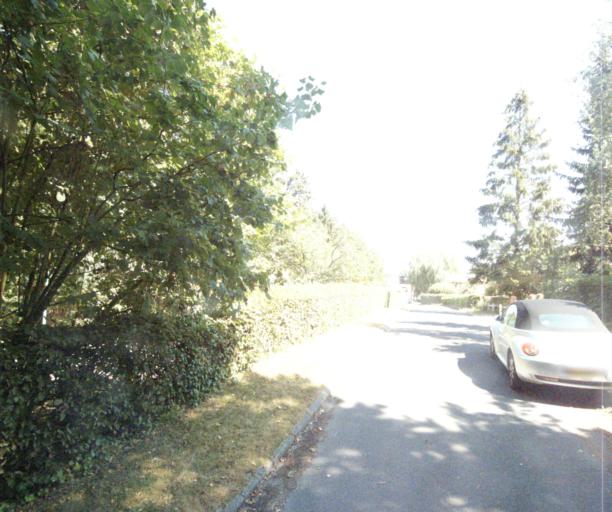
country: FR
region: Nord-Pas-de-Calais
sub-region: Departement du Nord
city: Neuville-en-Ferrain
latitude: 50.7636
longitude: 3.1435
